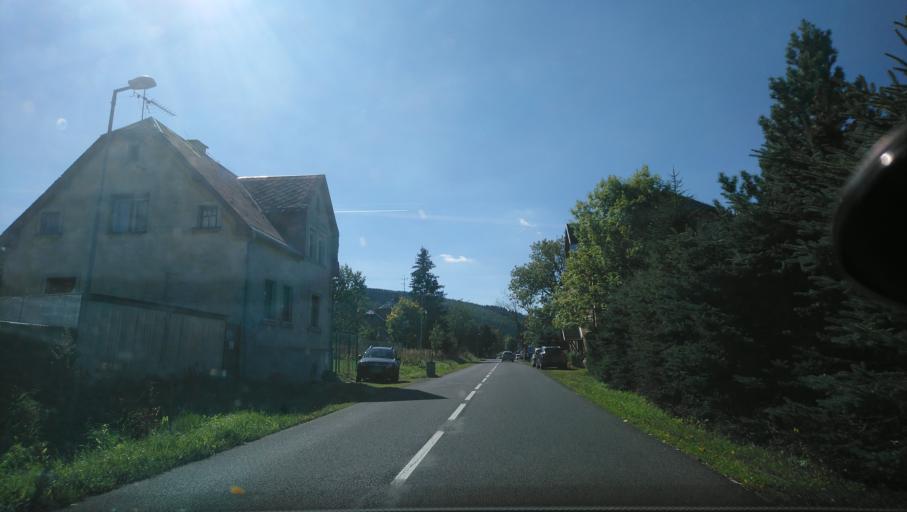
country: CZ
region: Ustecky
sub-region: Okres Chomutov
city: Kovarska
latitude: 50.4416
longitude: 13.0172
